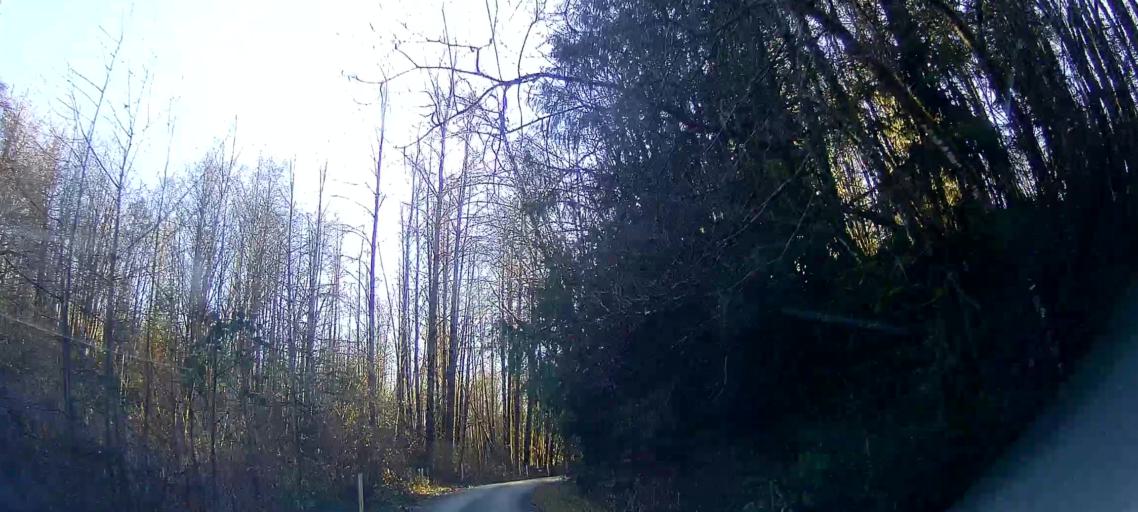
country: US
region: Washington
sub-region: Snohomish County
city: Darrington
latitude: 48.5425
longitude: -121.7271
